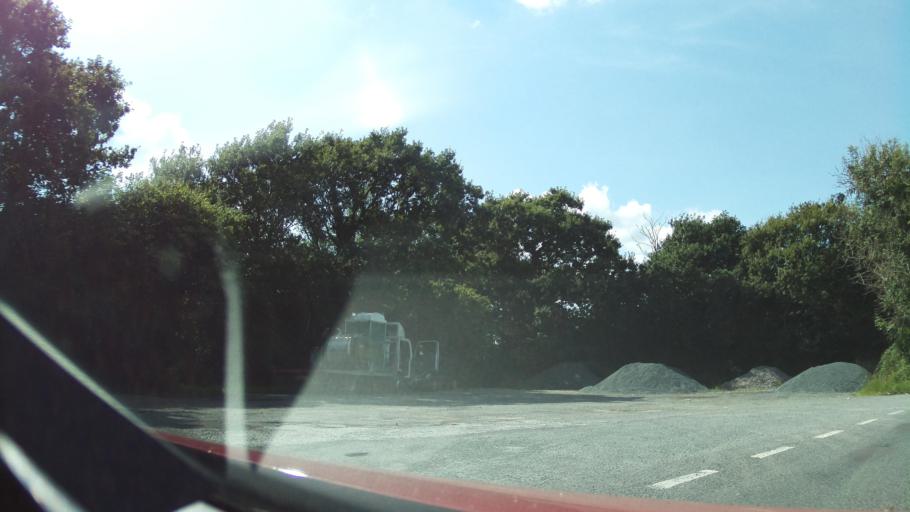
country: GB
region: England
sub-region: Cornwall
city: Saltash
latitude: 50.4234
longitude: -4.2426
